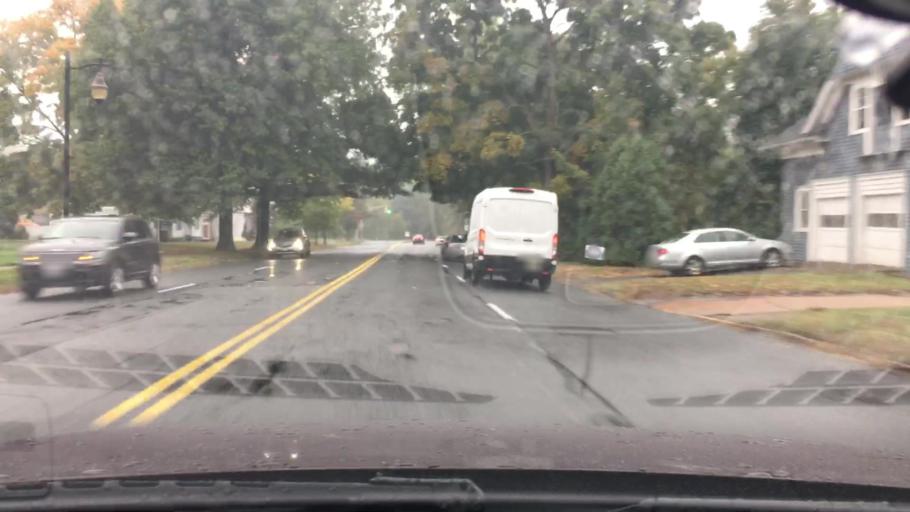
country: US
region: Massachusetts
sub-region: Hampden County
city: Springfield
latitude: 42.0804
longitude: -72.5757
